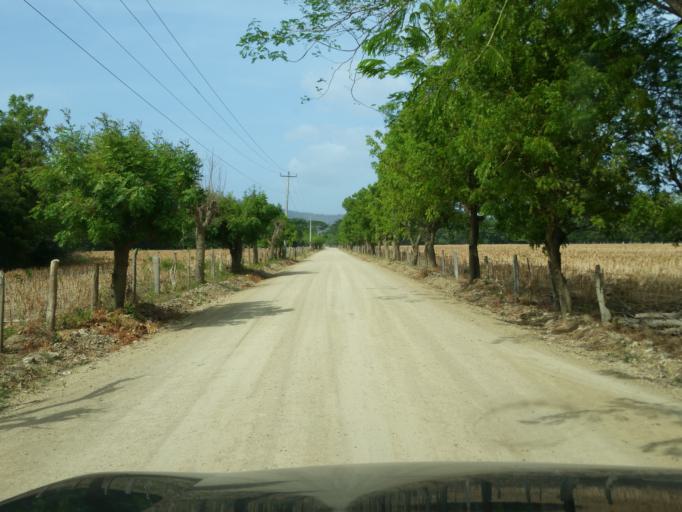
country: NI
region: Rivas
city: Tola
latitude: 11.4156
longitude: -86.0475
